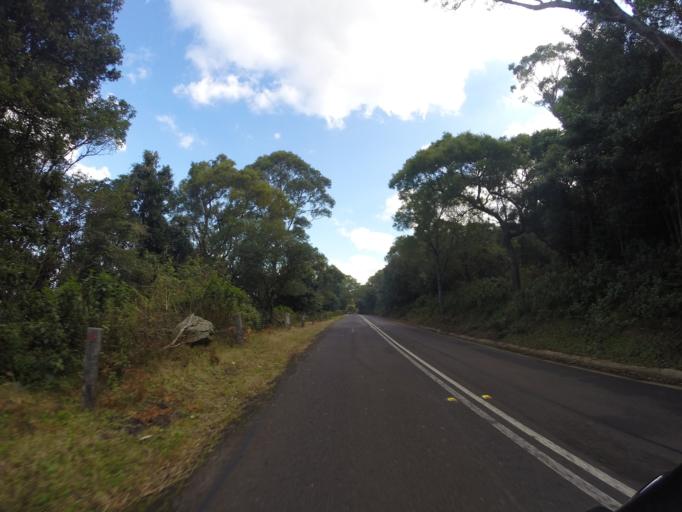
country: AU
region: New South Wales
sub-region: Wollongong
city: Mount Keira
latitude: -34.4063
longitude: 150.8567
